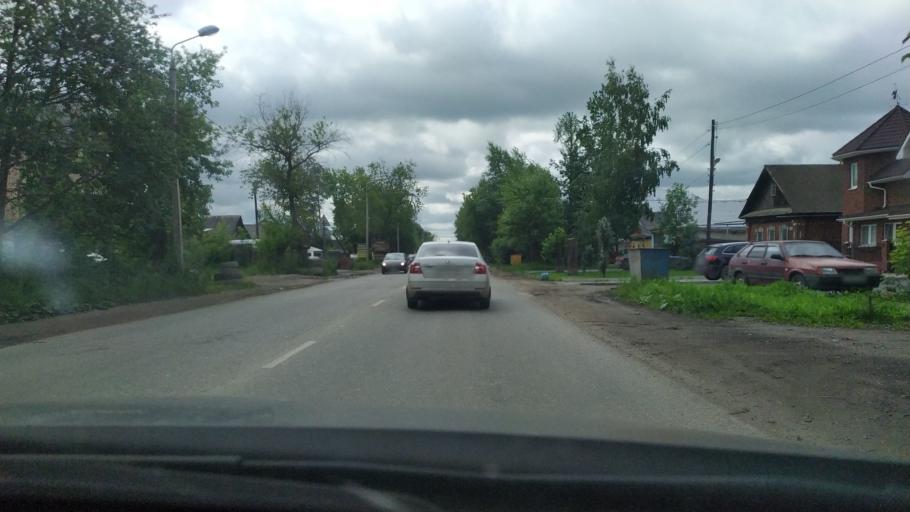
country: RU
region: Perm
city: Perm
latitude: 57.9810
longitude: 56.3049
